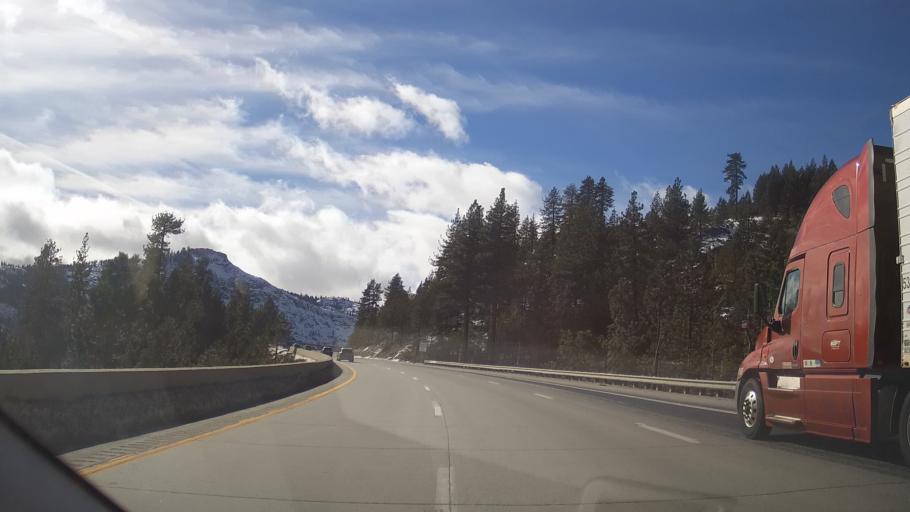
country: US
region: California
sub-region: Nevada County
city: Truckee
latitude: 39.3307
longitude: -120.2919
